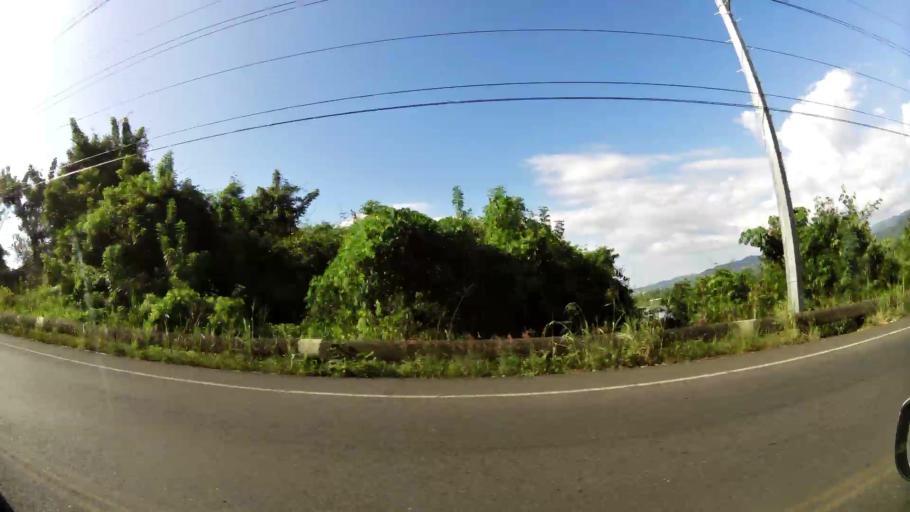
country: CR
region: Puntarenas
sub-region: Canton de Garabito
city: Jaco
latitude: 9.5959
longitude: -84.6201
